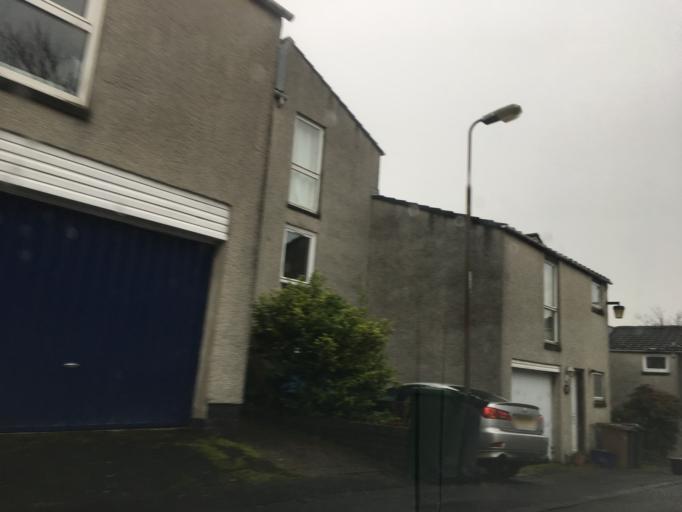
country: GB
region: Scotland
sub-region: Edinburgh
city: Currie
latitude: 55.9566
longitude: -3.3032
